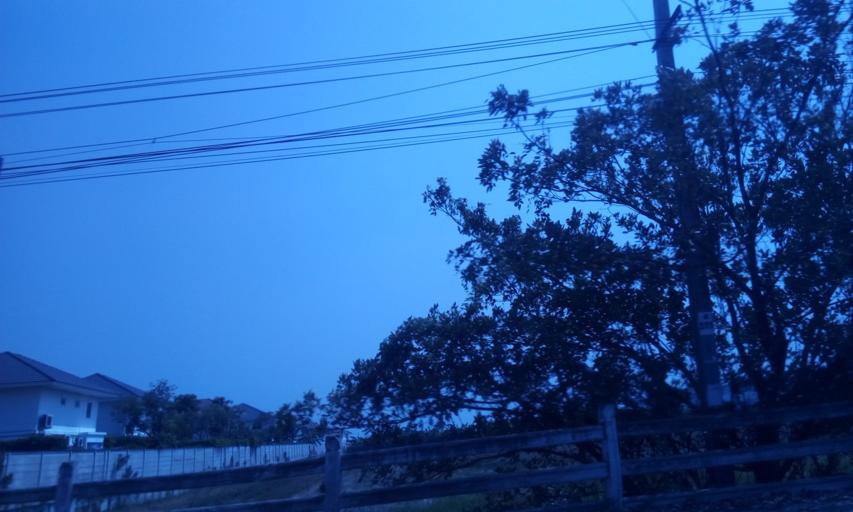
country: TH
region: Nonthaburi
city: Sai Noi
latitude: 13.9096
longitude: 100.3292
